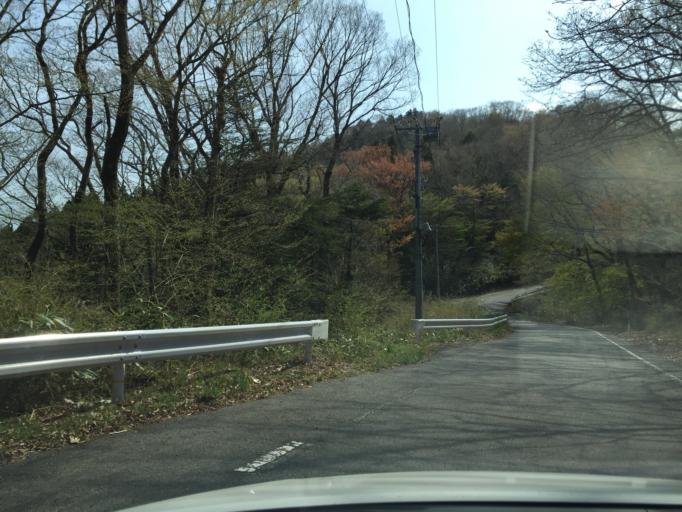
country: JP
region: Fukushima
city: Iwaki
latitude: 37.2027
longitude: 140.8560
